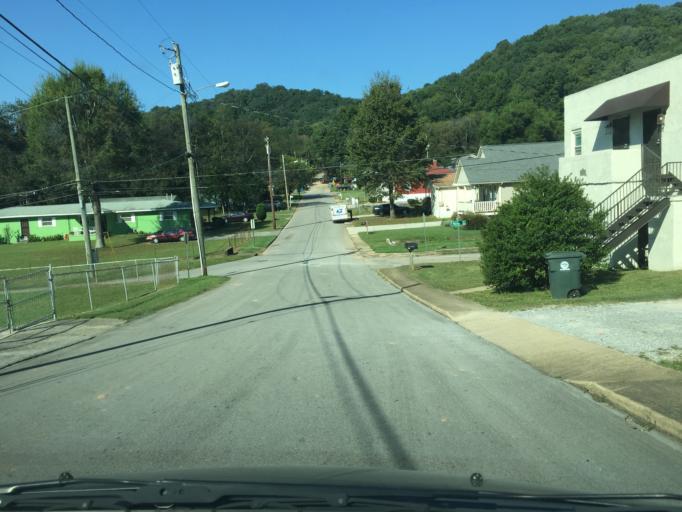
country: US
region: Tennessee
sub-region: Hamilton County
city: Chattanooga
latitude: 35.0744
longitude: -85.3079
